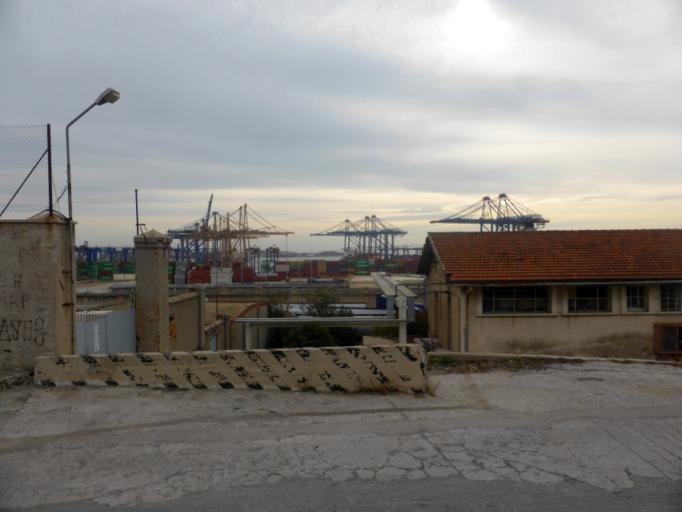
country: GR
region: Attica
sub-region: Nomos Piraios
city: Perama
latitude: 37.9630
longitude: 23.5883
